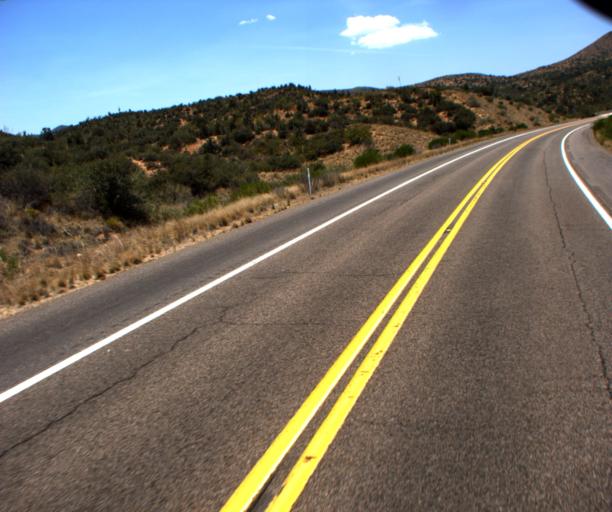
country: US
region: Arizona
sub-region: Gila County
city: Claypool
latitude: 33.5242
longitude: -110.9064
